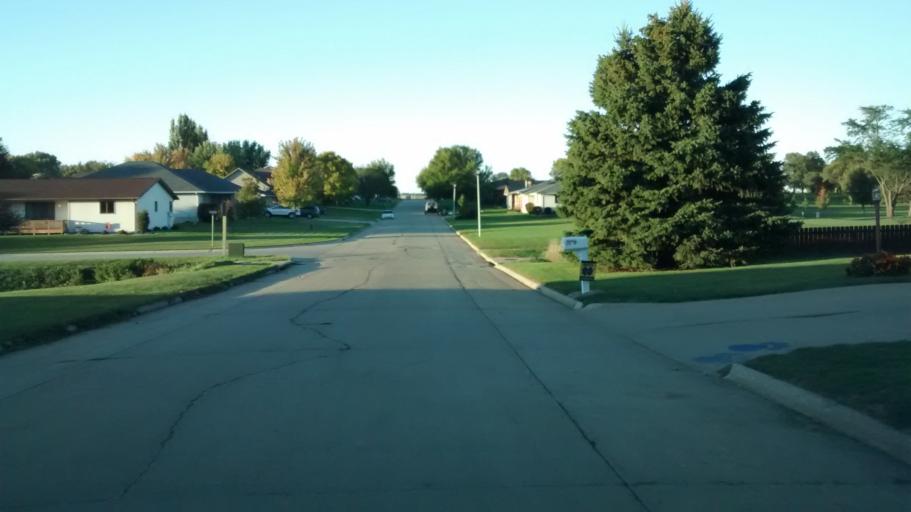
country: US
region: Iowa
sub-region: Woodbury County
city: Moville
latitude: 42.4927
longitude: -96.0666
